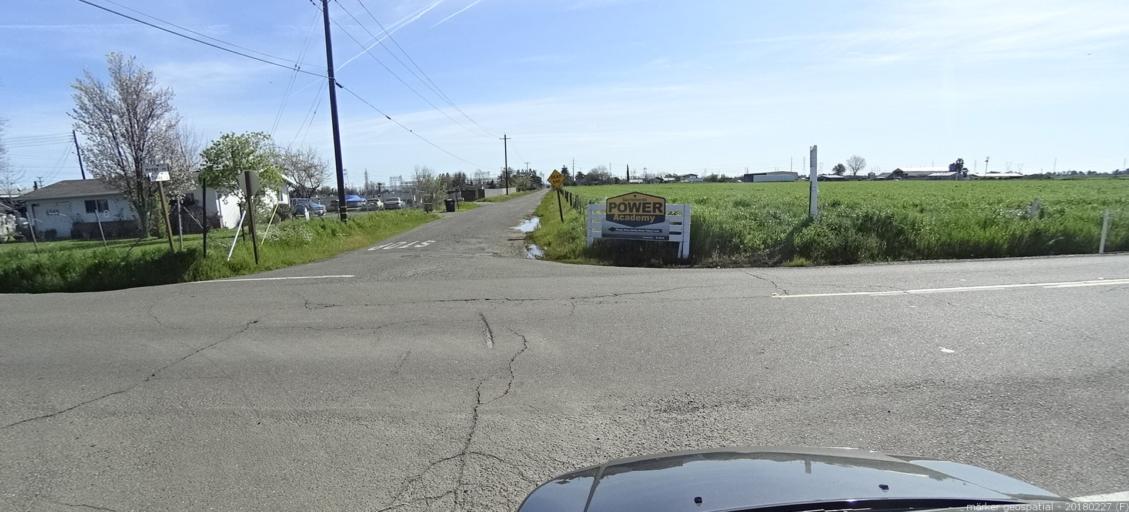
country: US
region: California
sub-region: Sacramento County
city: Rosemont
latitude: 38.5071
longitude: -121.3628
